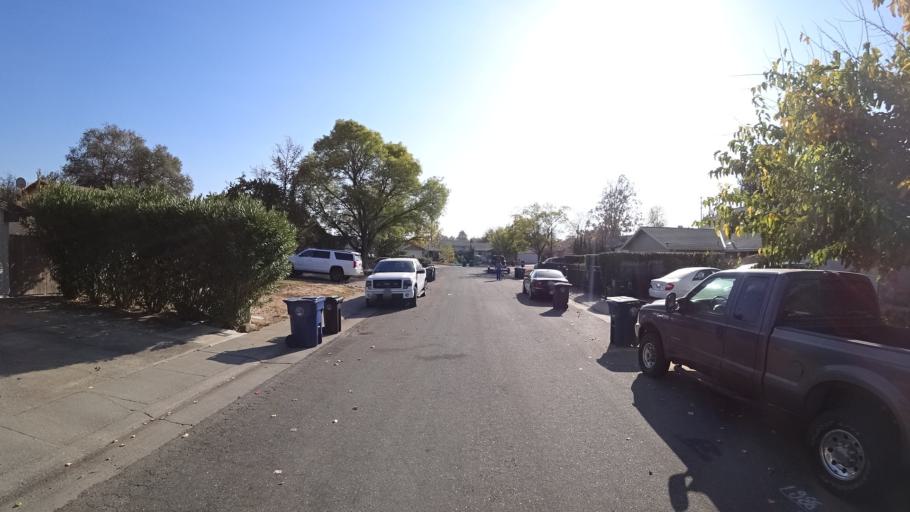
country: US
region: California
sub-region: Sacramento County
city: Citrus Heights
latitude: 38.6866
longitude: -121.2745
